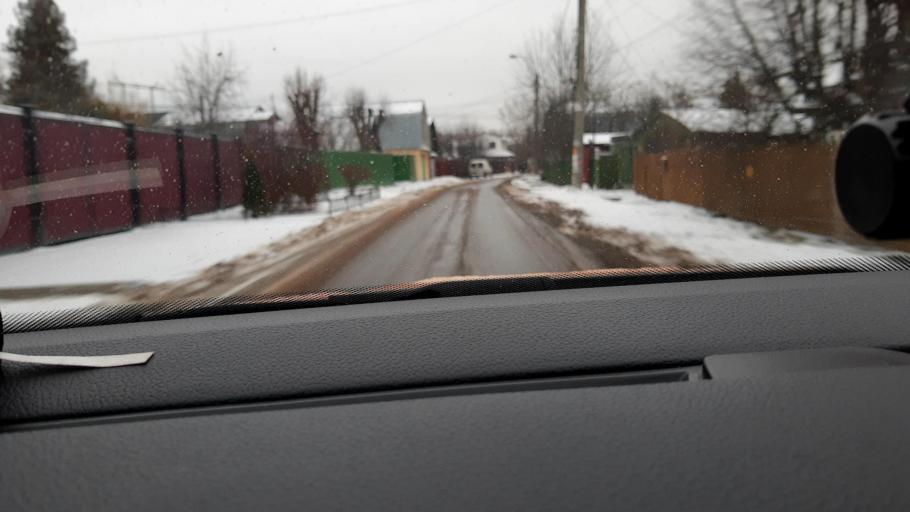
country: RU
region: Moskovskaya
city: Pirogovskiy
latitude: 55.9691
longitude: 37.7132
